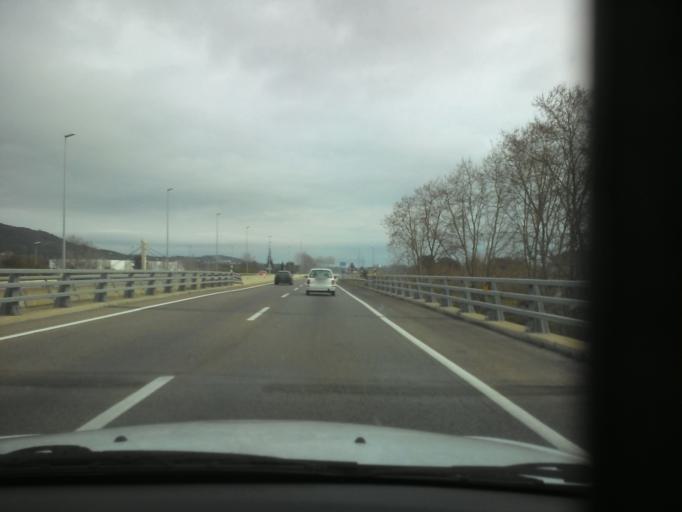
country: ES
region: Catalonia
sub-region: Provincia de Girona
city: Sant Feliu de Guixols
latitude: 41.8085
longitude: 3.0349
